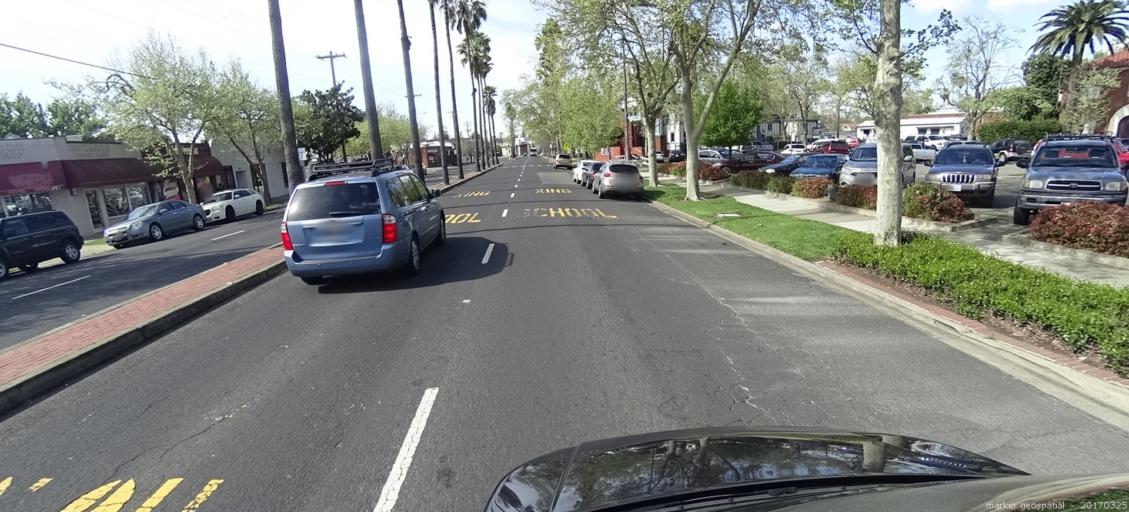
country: US
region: California
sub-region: Sacramento County
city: Sacramento
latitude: 38.5541
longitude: -121.4706
